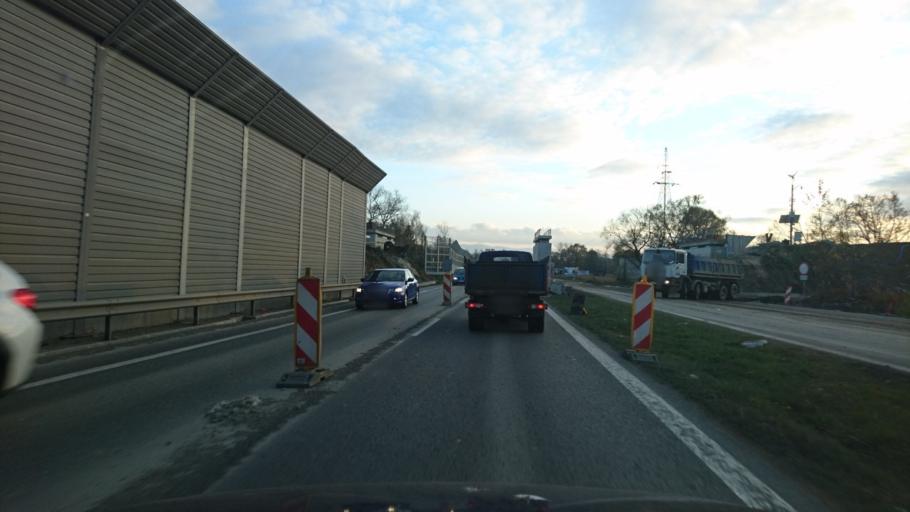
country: PL
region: Silesian Voivodeship
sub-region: Powiat bielski
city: Czechowice-Dziedzice
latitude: 49.9138
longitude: 18.9888
